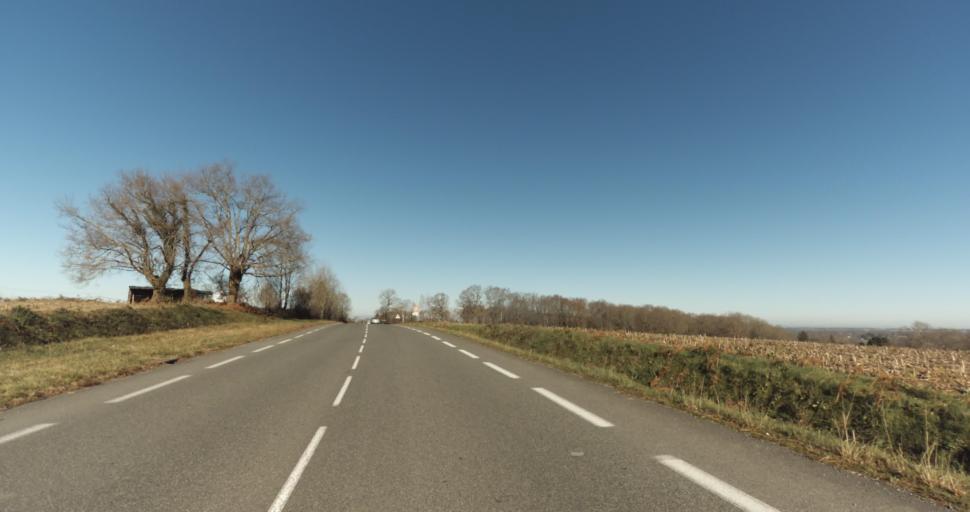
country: FR
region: Aquitaine
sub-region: Departement des Pyrenees-Atlantiques
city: Morlaas
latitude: 43.3415
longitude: -0.2756
